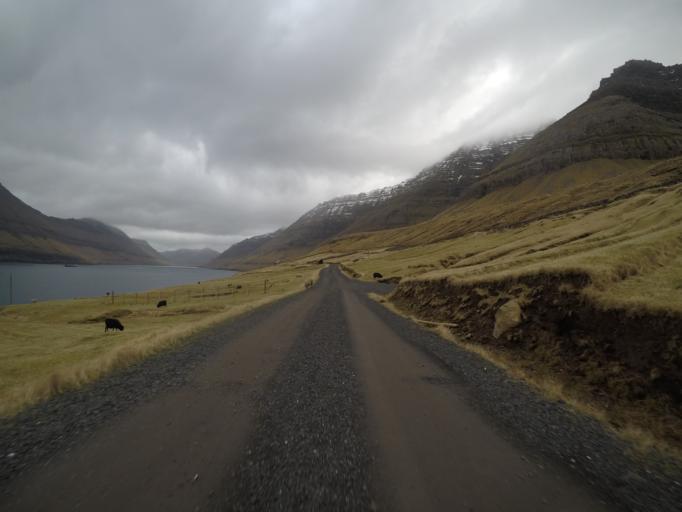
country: FO
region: Nordoyar
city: Klaksvik
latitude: 62.3500
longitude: -6.5823
